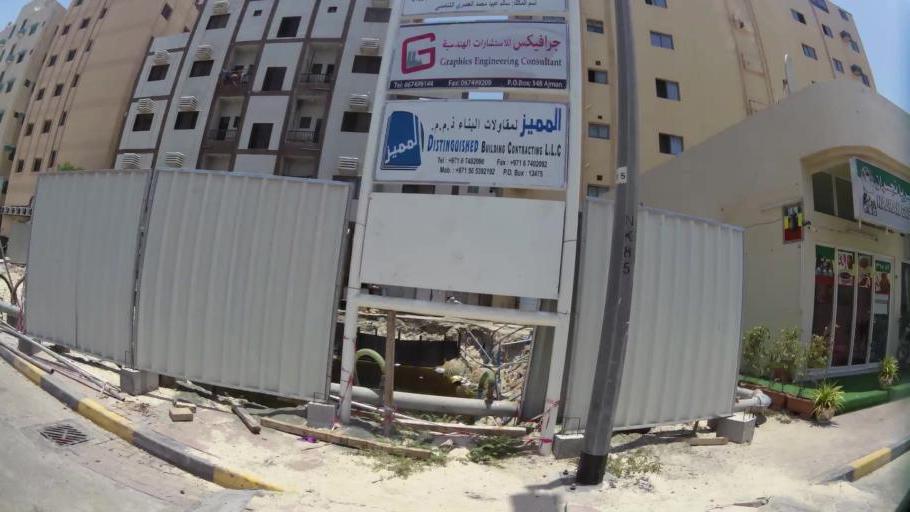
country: AE
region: Ajman
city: Ajman
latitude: 25.4119
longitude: 55.4379
